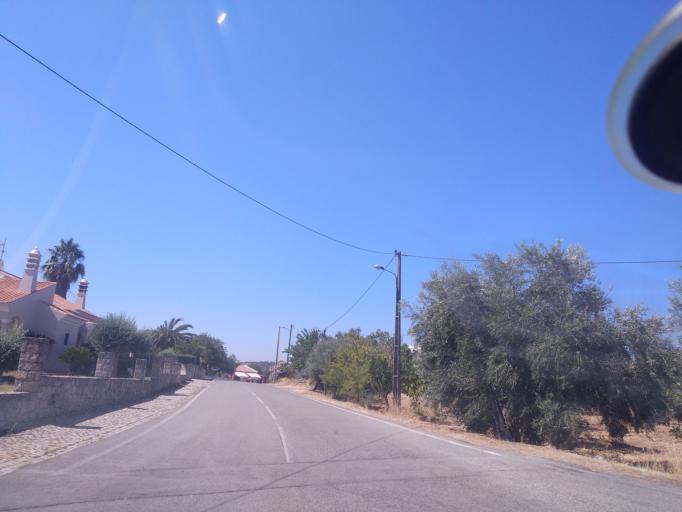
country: PT
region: Faro
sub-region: Sao Bras de Alportel
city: Sao Bras de Alportel
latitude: 37.1595
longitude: -7.9349
